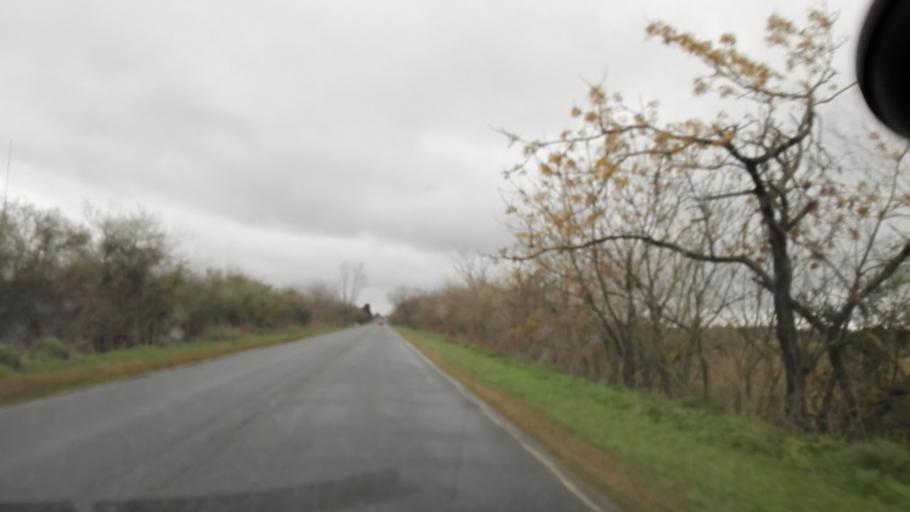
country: AR
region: Buenos Aires
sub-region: Partido de Brandsen
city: Brandsen
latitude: -35.1775
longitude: -58.2516
